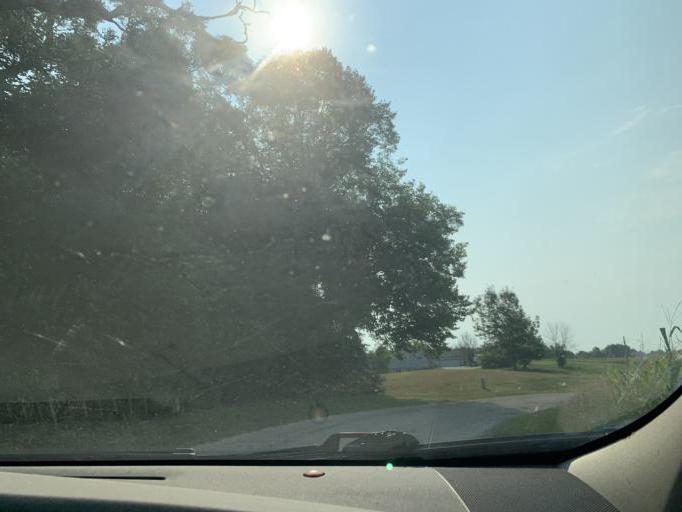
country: US
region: Illinois
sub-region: Whiteside County
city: Morrison
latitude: 41.8598
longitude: -89.8721
